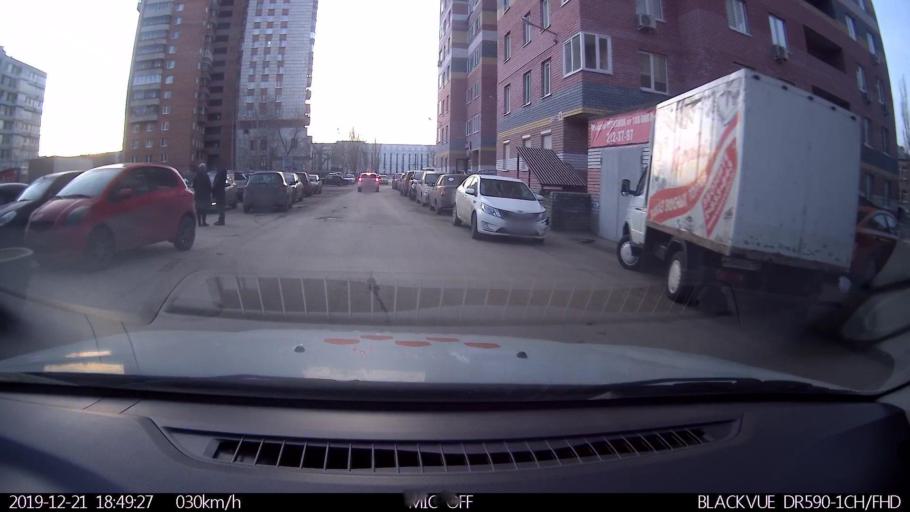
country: RU
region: Nizjnij Novgorod
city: Nizhniy Novgorod
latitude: 56.3220
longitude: 43.9313
